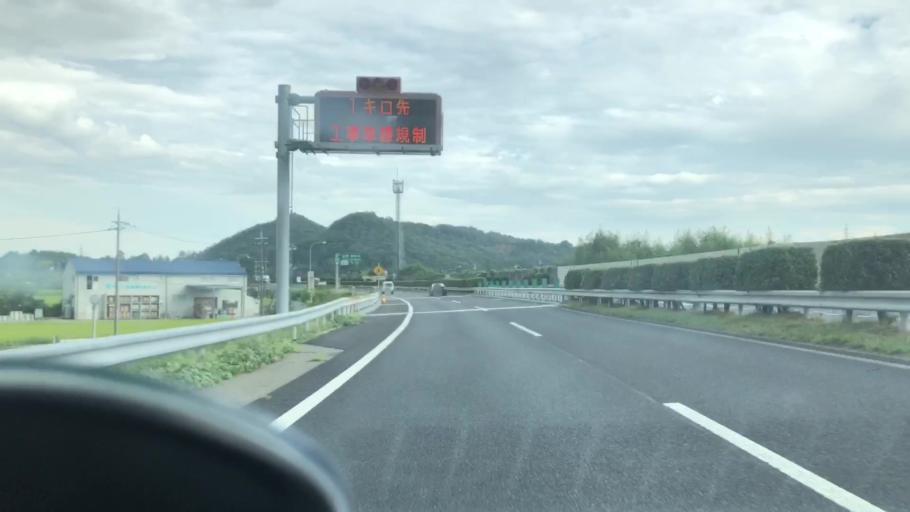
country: JP
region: Hyogo
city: Yashiro
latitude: 34.9354
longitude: 134.8602
